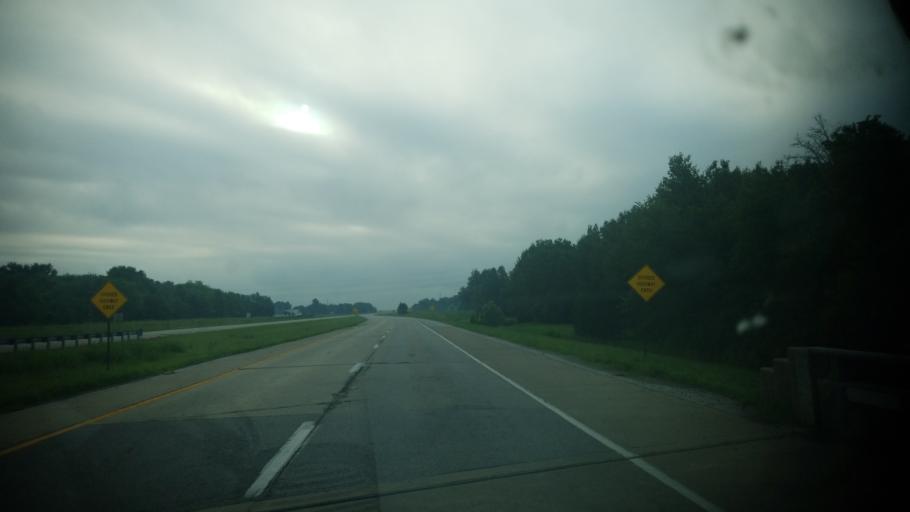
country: US
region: Illinois
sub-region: Clay County
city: Flora
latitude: 38.6746
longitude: -88.4357
